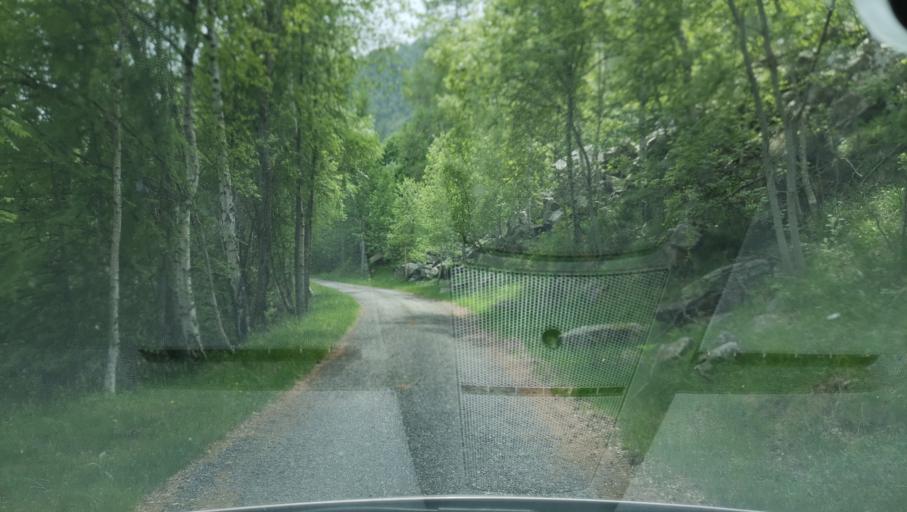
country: IT
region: Piedmont
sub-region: Provincia di Torino
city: Quincinetto
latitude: 45.5379
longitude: 7.7896
